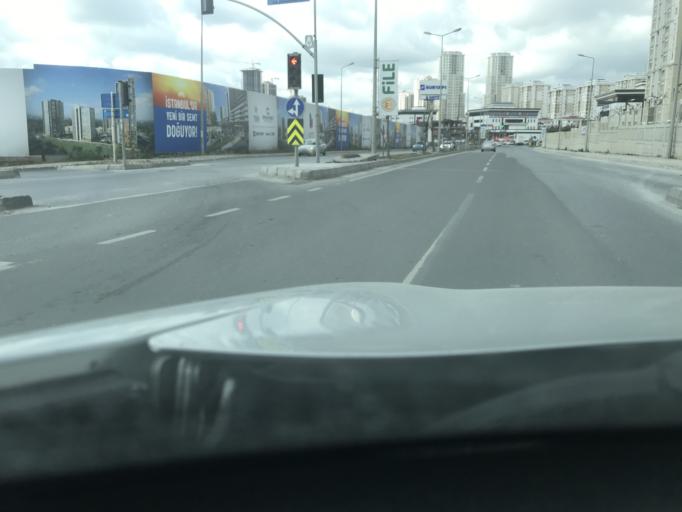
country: TR
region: Istanbul
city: Esenyurt
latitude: 41.0842
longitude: 28.6524
